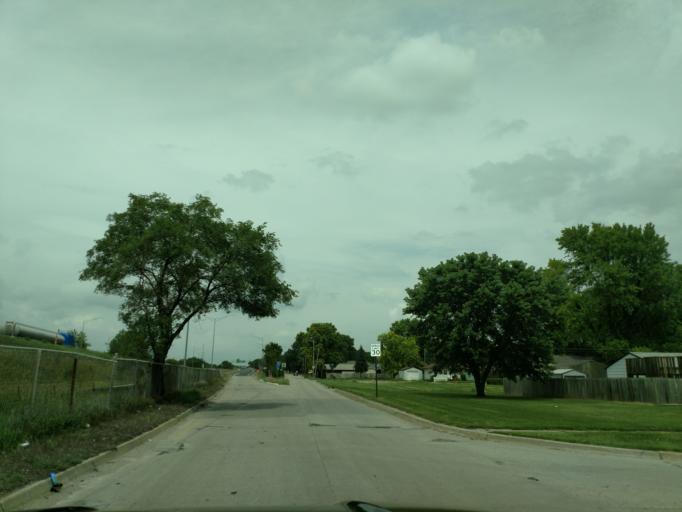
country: US
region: Nebraska
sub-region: Douglas County
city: Omaha
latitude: 41.2545
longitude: -95.9064
